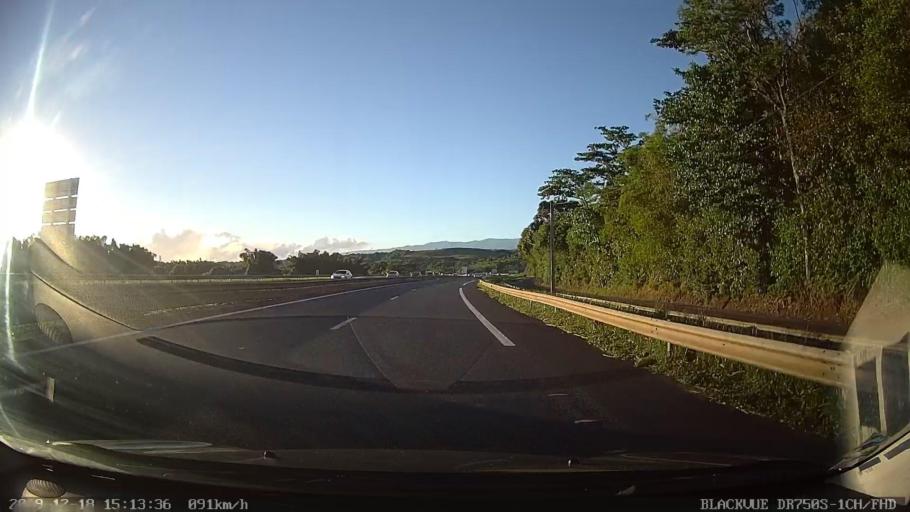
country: RE
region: Reunion
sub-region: Reunion
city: Sainte-Suzanne
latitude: -20.9222
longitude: 55.6259
